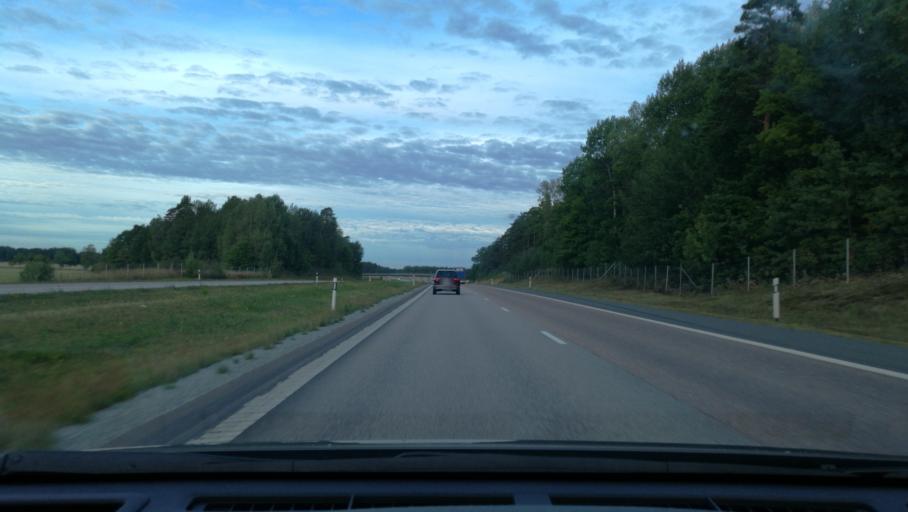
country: SE
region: OErebro
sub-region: Orebro Kommun
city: Hovsta
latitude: 59.3073
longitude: 15.3487
